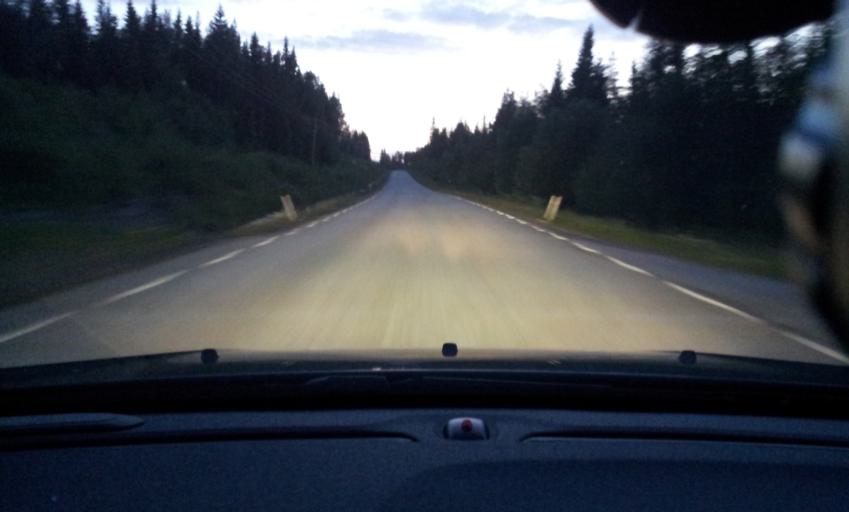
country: SE
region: Jaemtland
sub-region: Bergs Kommun
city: Hoverberg
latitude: 62.6636
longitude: 14.7334
